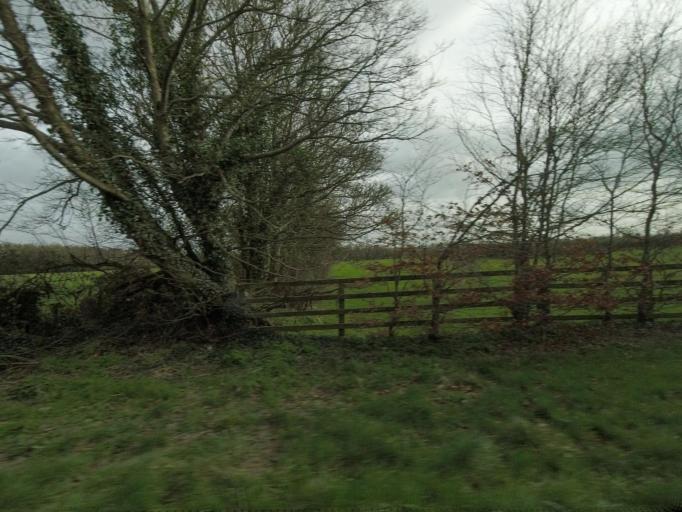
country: IE
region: Leinster
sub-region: Kildare
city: Kilcullen
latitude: 53.1555
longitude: -6.7078
